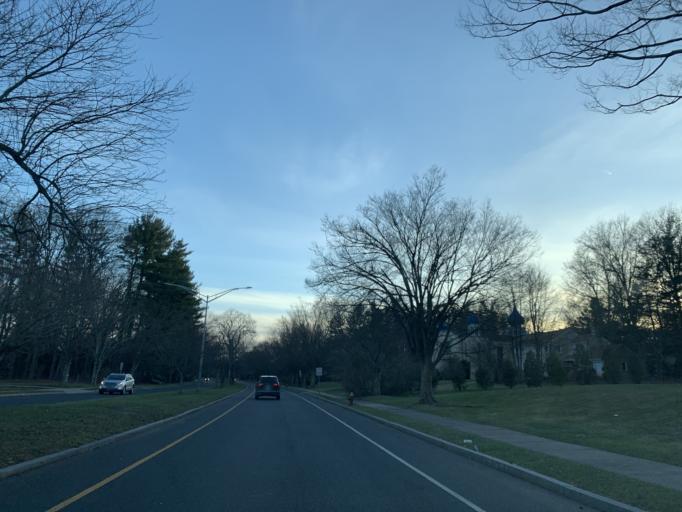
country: US
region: Connecticut
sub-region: Hartford County
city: Blue Hills
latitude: 41.7843
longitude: -72.7088
